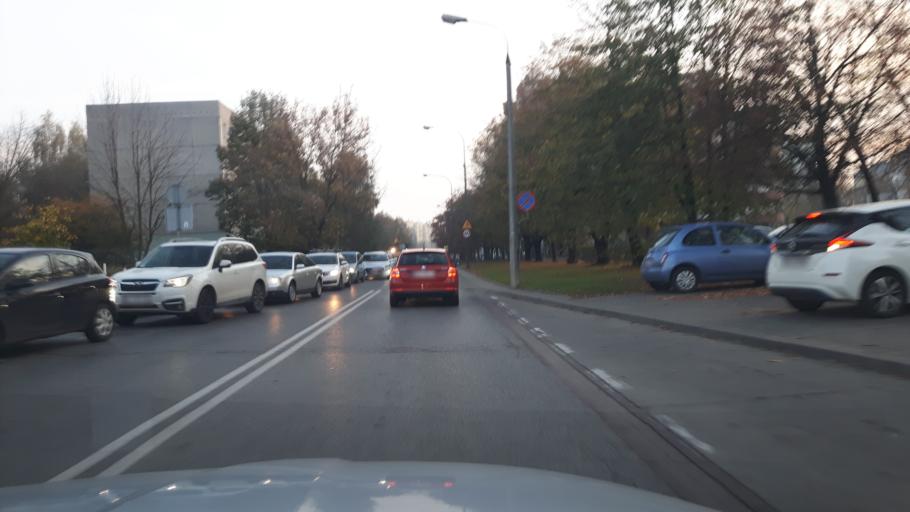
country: PL
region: Masovian Voivodeship
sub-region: Warszawa
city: Mokotow
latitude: 52.1829
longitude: 21.0141
